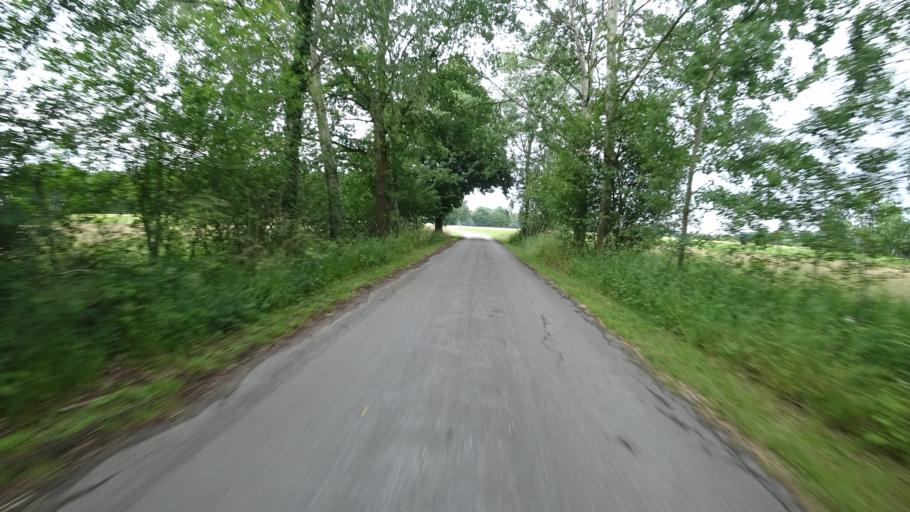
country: DE
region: North Rhine-Westphalia
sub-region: Regierungsbezirk Detmold
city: Guetersloh
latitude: 51.9490
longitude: 8.3296
